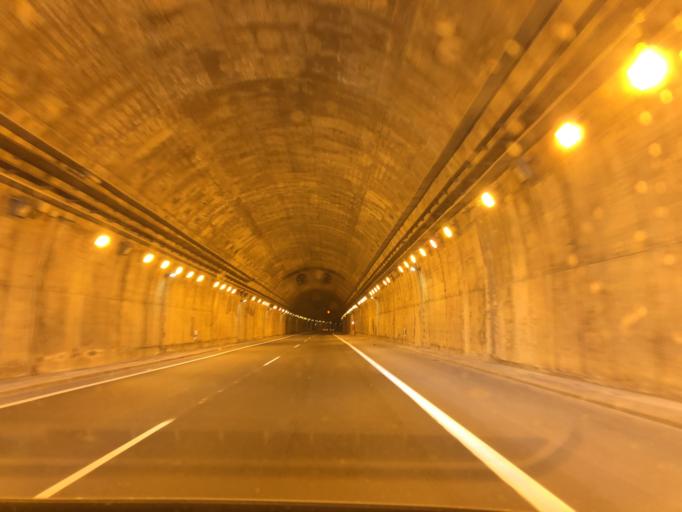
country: ES
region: Andalusia
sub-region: Provincia de Malaga
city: Estepona
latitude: 36.4279
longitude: -5.2026
